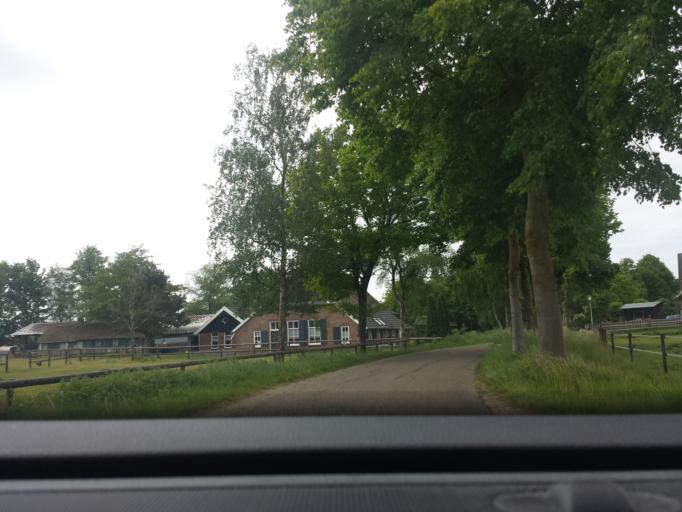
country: NL
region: Gelderland
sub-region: Oost Gelre
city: Lichtenvoorde
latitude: 52.0359
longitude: 6.5930
